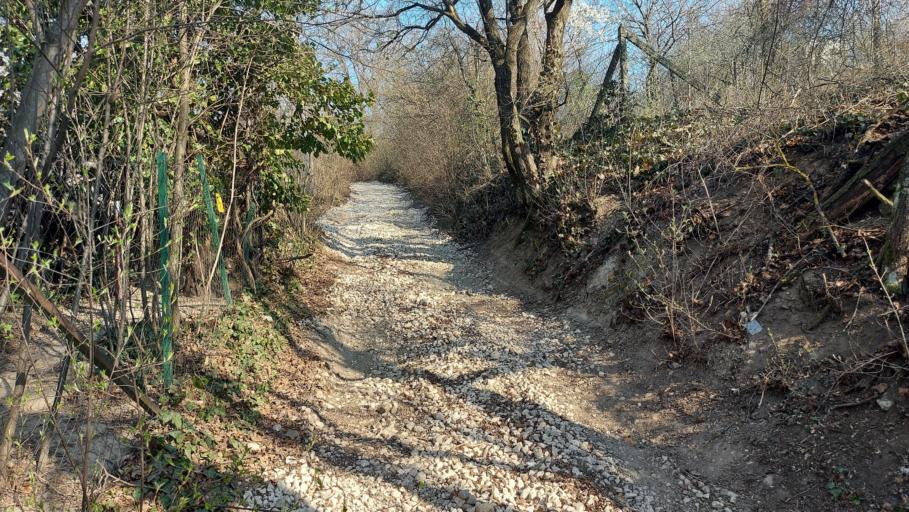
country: HU
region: Pest
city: Diosd
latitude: 47.4328
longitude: 18.9642
